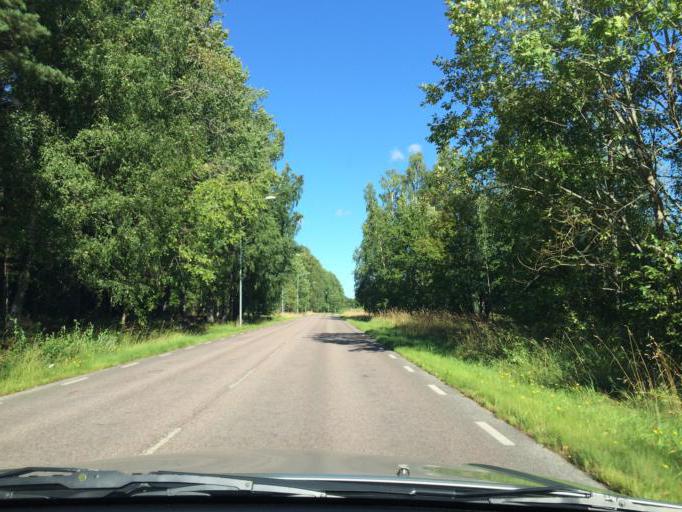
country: SE
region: Vaestmanland
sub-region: Vasteras
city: Vasteras
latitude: 59.5851
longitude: 16.6173
